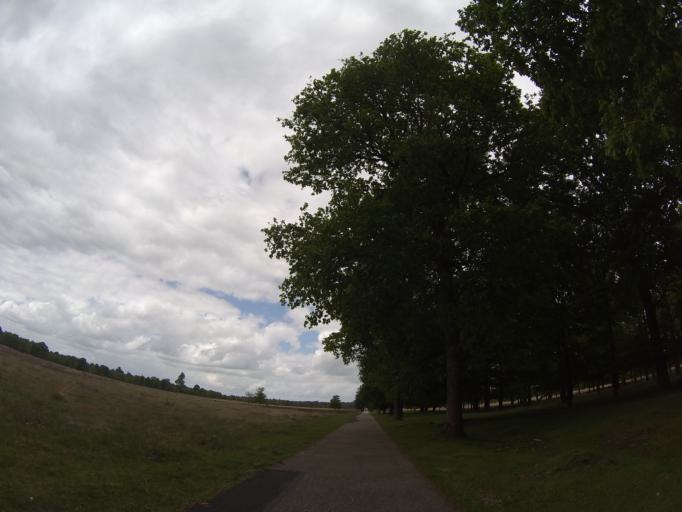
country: NL
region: Drenthe
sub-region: Gemeente Borger-Odoorn
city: Borger
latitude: 52.8580
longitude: 6.8085
